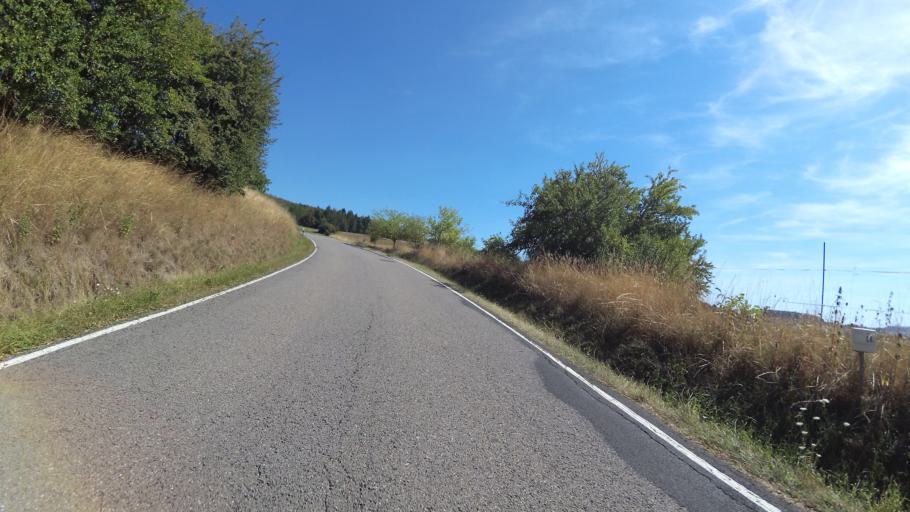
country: DE
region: Rheinland-Pfalz
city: Hornbach
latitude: 49.1667
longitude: 7.3150
